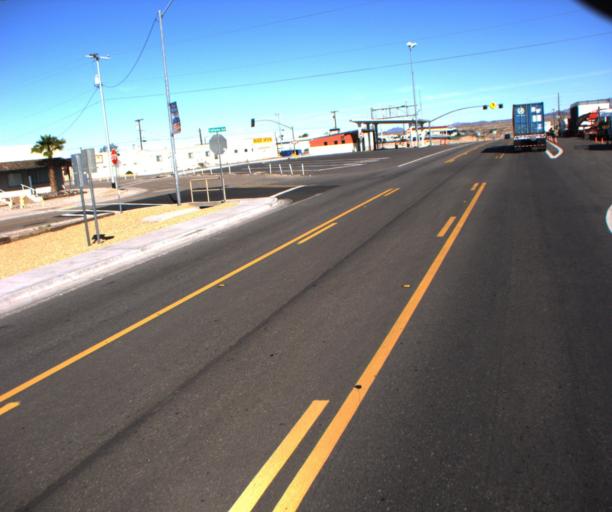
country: US
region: Arizona
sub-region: La Paz County
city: Parker
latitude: 34.1555
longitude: -114.2934
